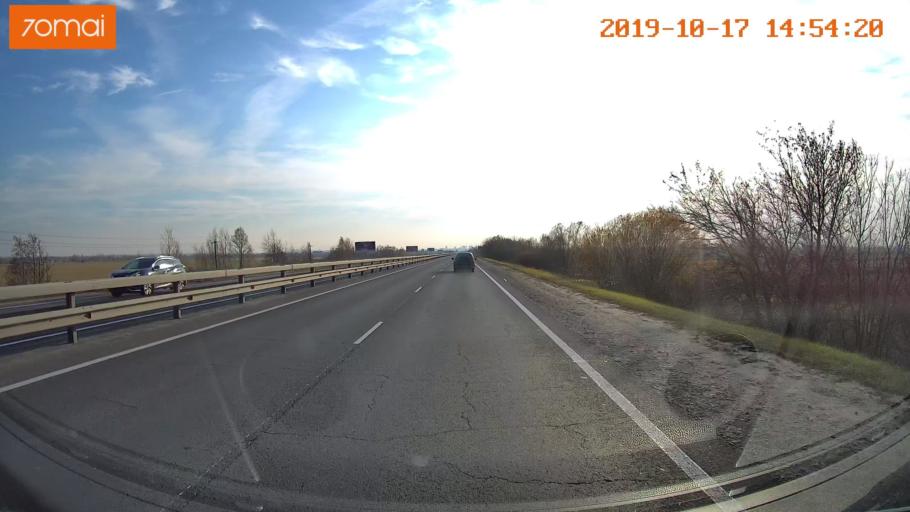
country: RU
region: Rjazan
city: Polyany
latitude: 54.6828
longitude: 39.8328
